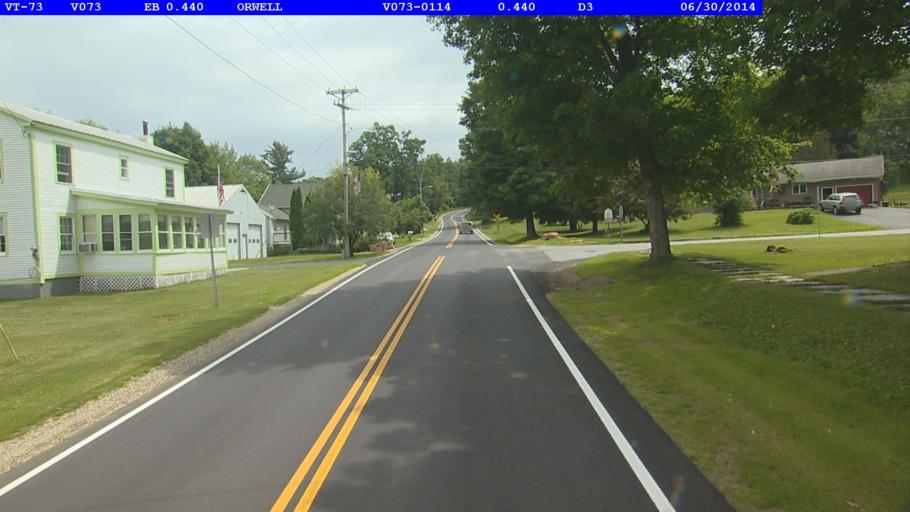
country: US
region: New York
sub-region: Essex County
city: Ticonderoga
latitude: 43.8039
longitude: -73.2962
